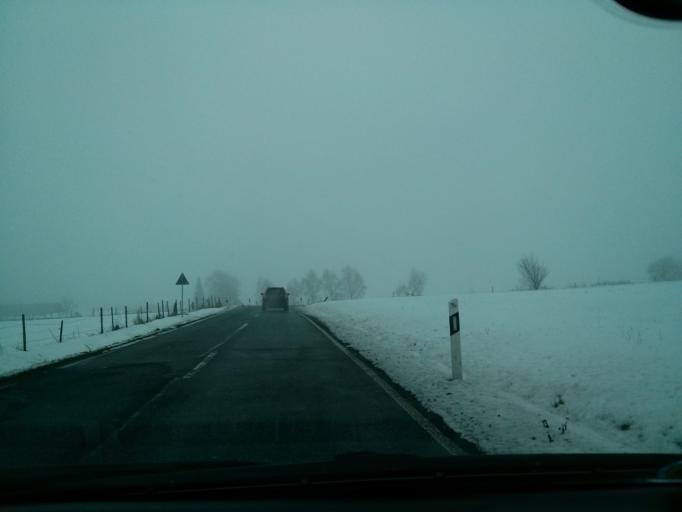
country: DE
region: Rheinland-Pfalz
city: Berg
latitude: 50.5753
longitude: 6.9461
